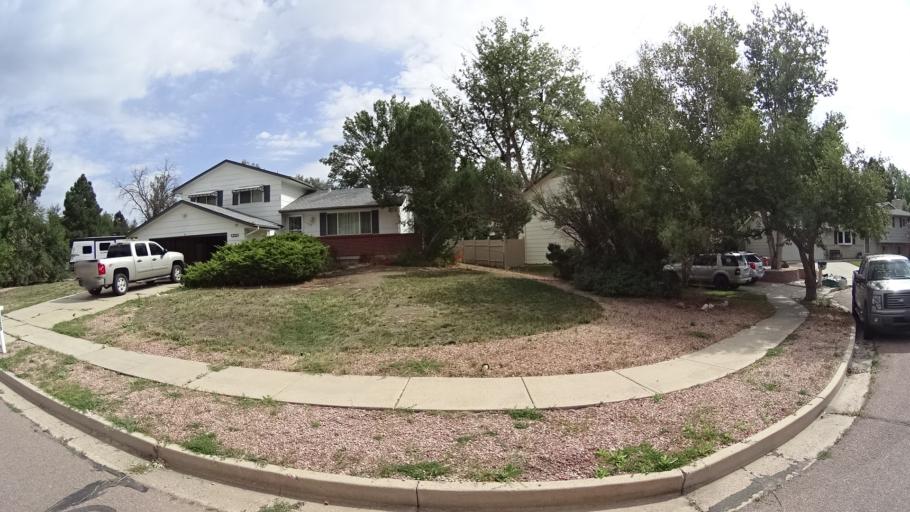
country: US
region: Colorado
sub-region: El Paso County
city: Cimarron Hills
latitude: 38.8582
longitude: -104.7331
